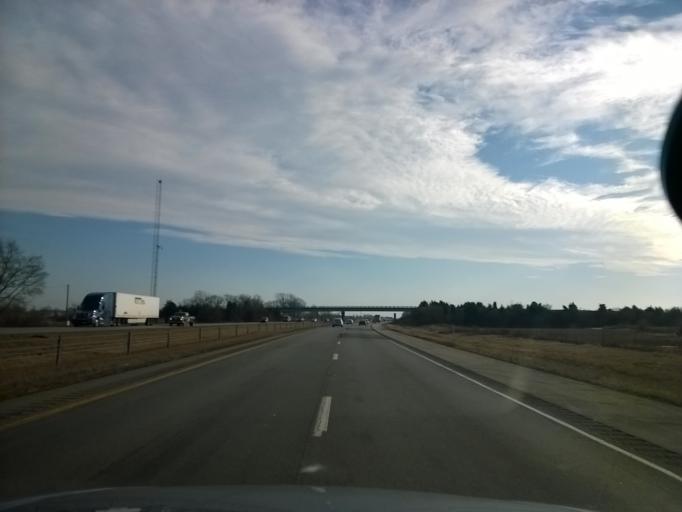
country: US
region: Indiana
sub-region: Johnson County
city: Franklin
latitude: 39.5237
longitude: -86.0256
